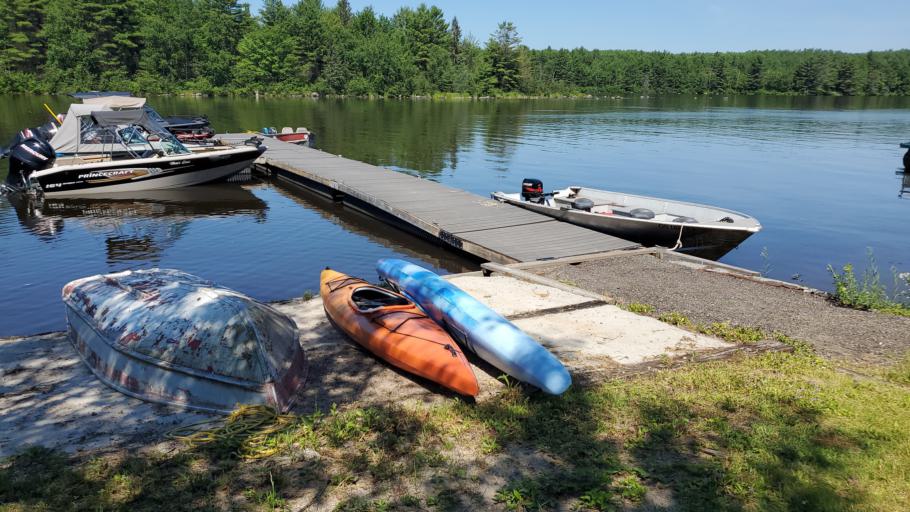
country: CA
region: Ontario
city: Mattawa
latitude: 46.2577
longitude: -78.2764
